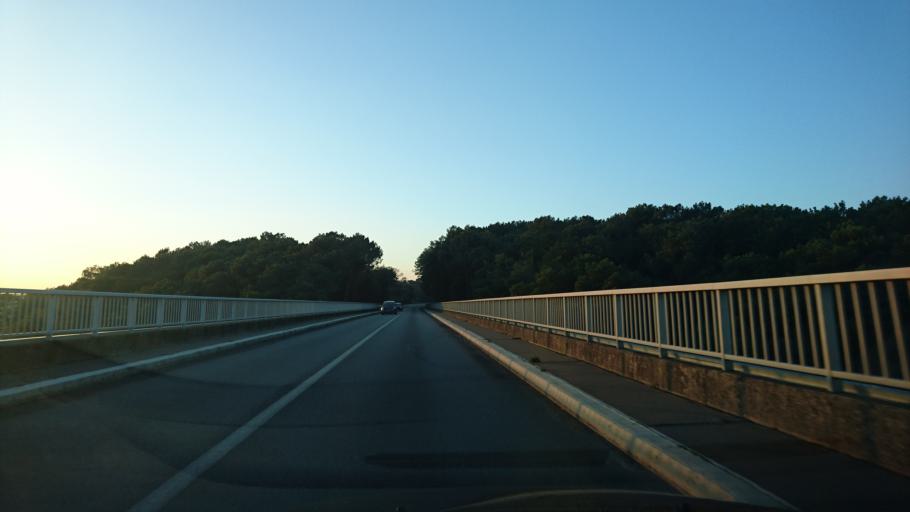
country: FR
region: Brittany
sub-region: Departement du Morbihan
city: Le Bono
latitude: 47.6391
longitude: -2.9554
